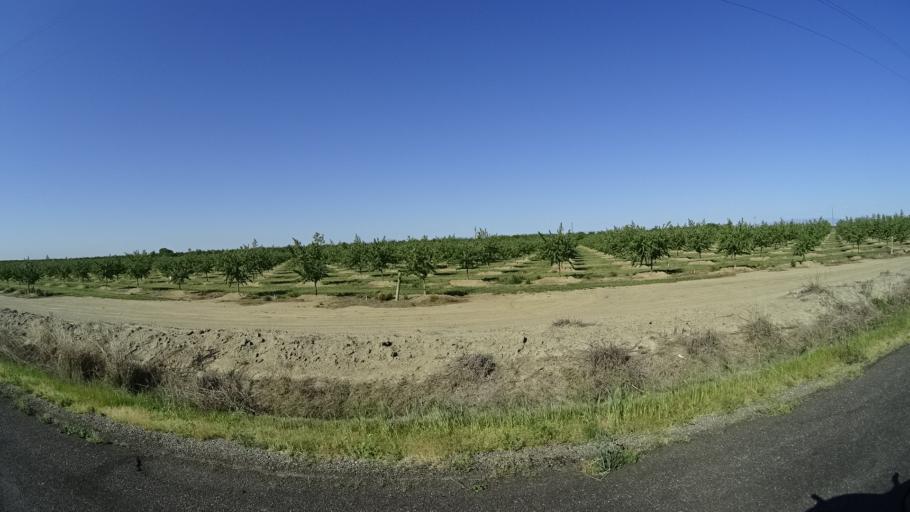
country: US
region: California
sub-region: Glenn County
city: Hamilton City
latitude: 39.7061
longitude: -122.0764
